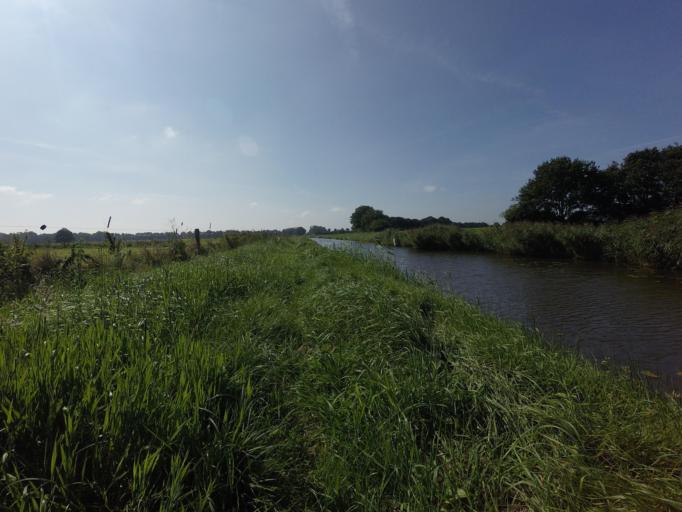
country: NL
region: Drenthe
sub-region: Gemeente Tynaarlo
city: Vries
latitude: 53.1207
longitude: 6.5268
